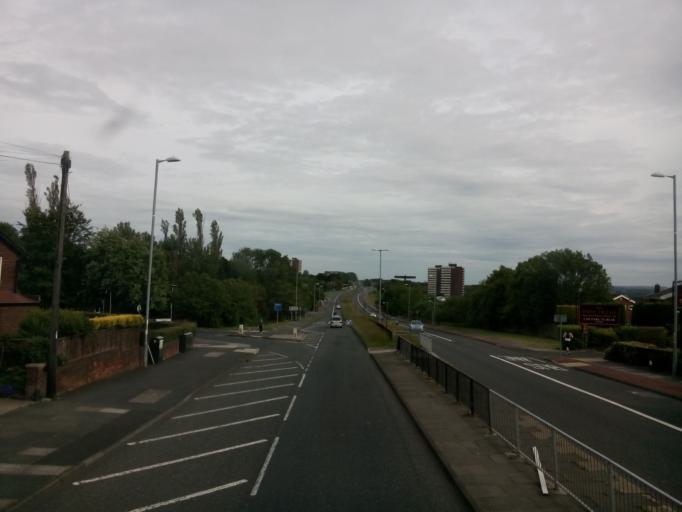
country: GB
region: England
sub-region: Gateshead
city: Lamesley
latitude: 54.9262
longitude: -1.5950
